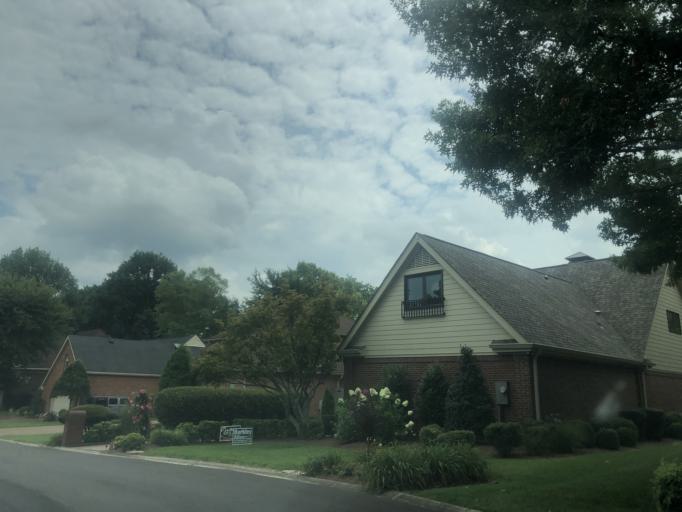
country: US
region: Tennessee
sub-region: Davidson County
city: Oak Hill
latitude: 36.0925
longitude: -86.8048
